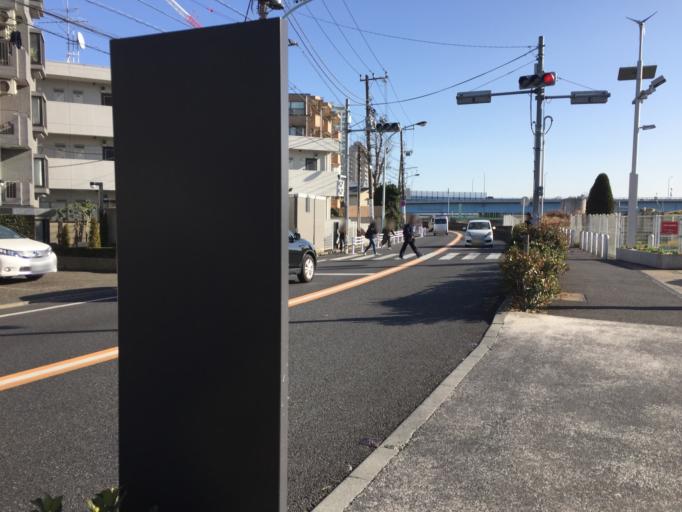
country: JP
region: Tokyo
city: Chofugaoka
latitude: 35.6148
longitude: 139.6221
